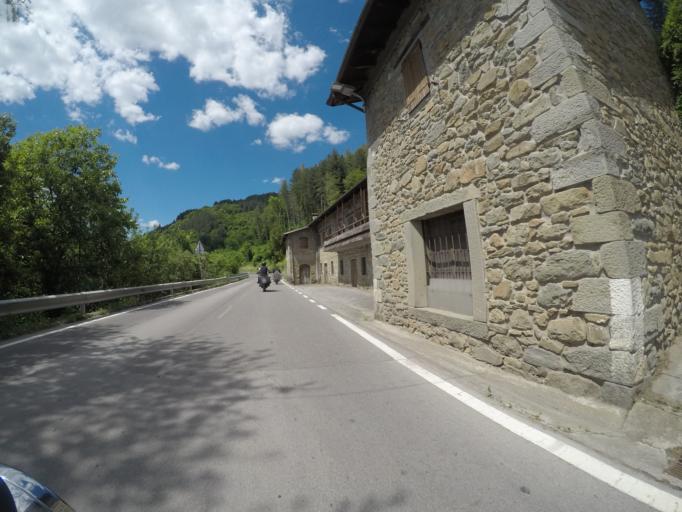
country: IT
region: Tuscany
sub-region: Provincia di Lucca
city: San Romano in Garfagnana
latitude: 44.1660
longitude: 10.3527
